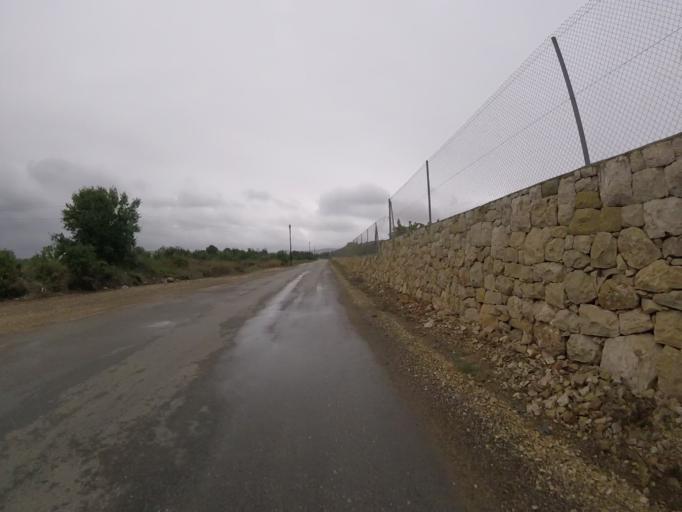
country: ES
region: Valencia
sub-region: Provincia de Castello
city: Alcoceber
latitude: 40.2404
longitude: 0.2493
